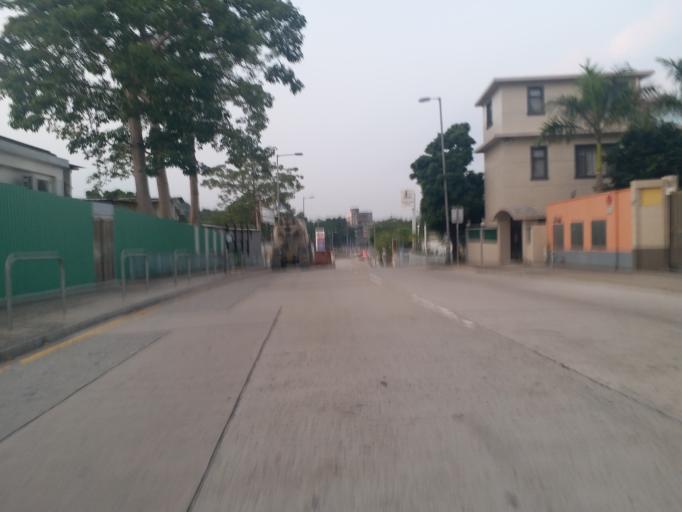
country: HK
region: Yuen Long
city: Yuen Long Kau Hui
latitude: 22.4400
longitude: 114.0111
